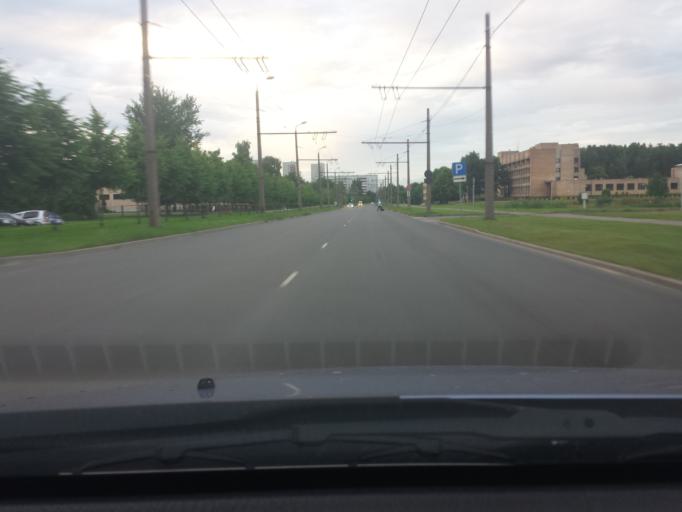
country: LV
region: Stopini
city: Ulbroka
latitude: 56.9602
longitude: 24.2384
